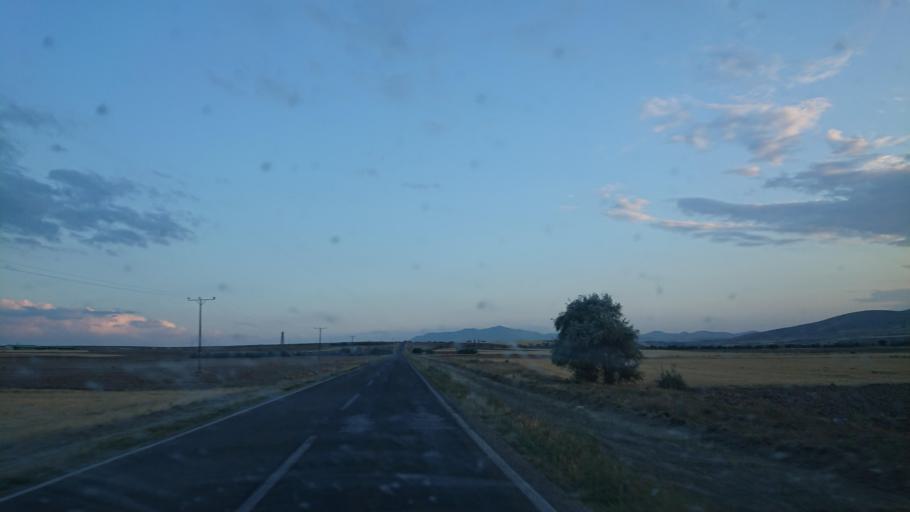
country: TR
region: Aksaray
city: Balci
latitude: 38.8094
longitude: 34.1321
